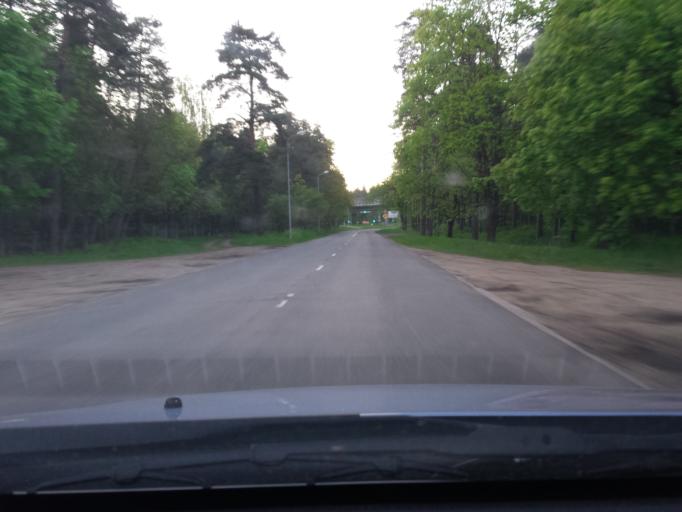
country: LV
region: Riga
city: Jaunciems
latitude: 56.9937
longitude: 24.1405
